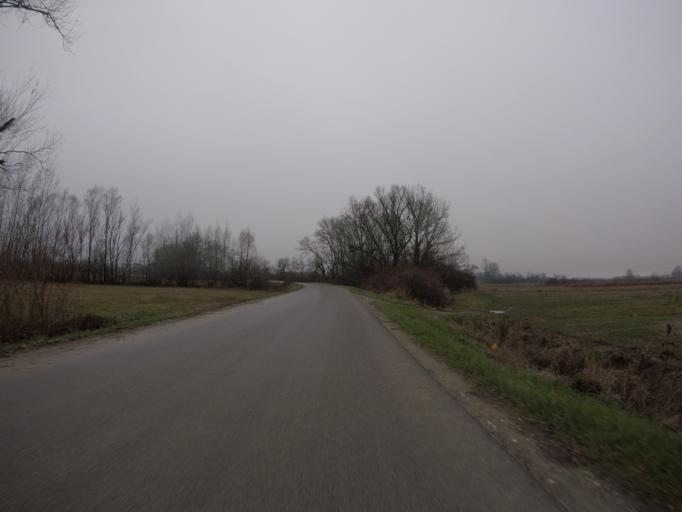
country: HR
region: Sisacko-Moslavacka
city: Lekenik
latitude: 45.6232
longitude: 16.3245
